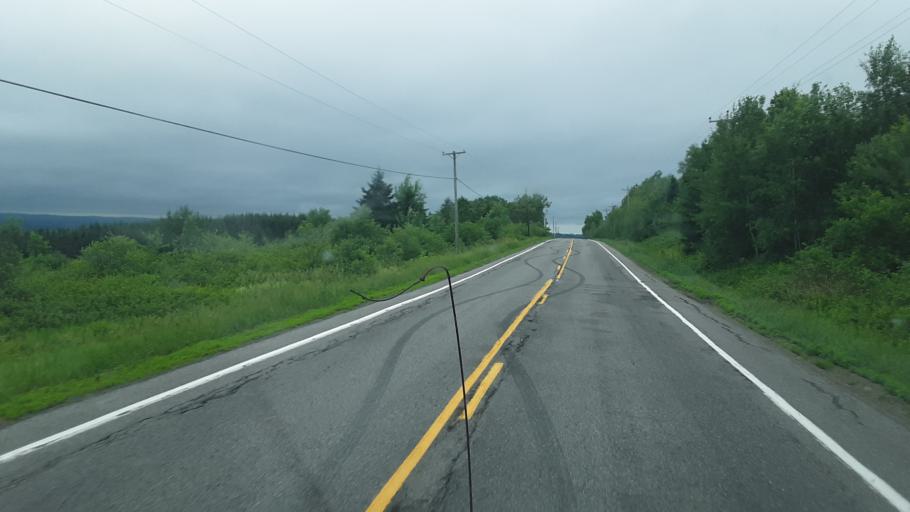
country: US
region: Maine
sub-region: Penobscot County
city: Patten
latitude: 46.0308
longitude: -68.4448
